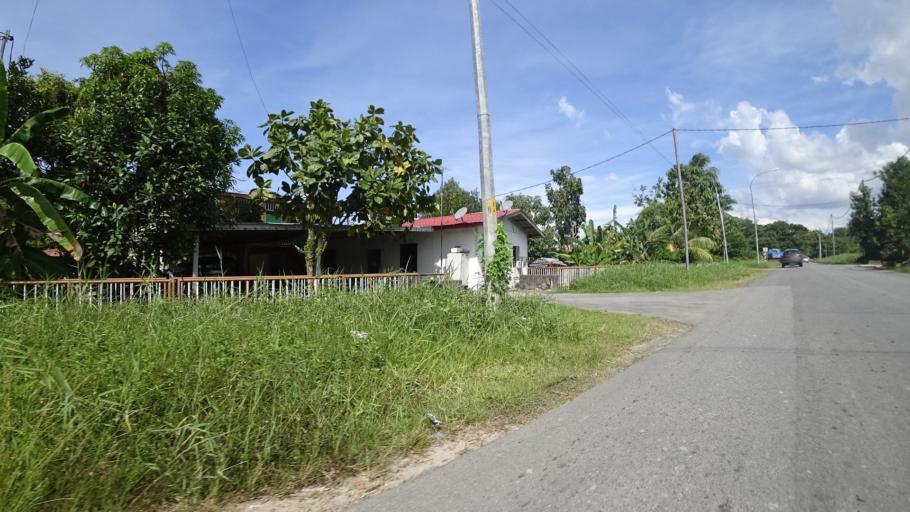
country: BN
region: Brunei and Muara
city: Bandar Seri Begawan
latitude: 4.8729
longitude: 114.8589
